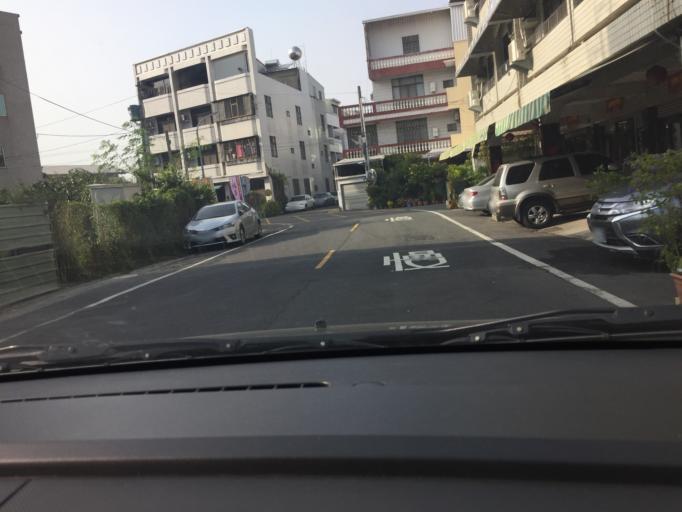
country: TW
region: Taiwan
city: Xinying
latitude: 23.1849
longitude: 120.2553
